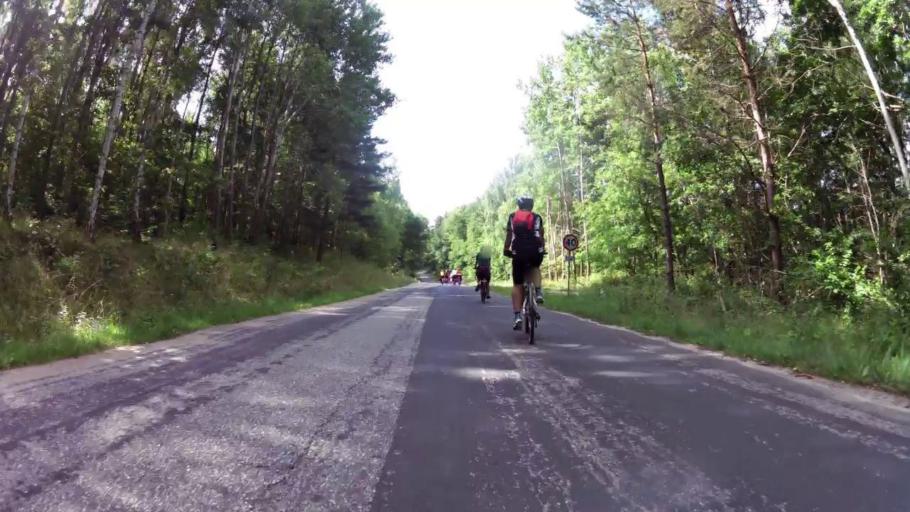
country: PL
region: West Pomeranian Voivodeship
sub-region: Powiat drawski
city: Drawsko Pomorskie
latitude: 53.4725
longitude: 15.7847
